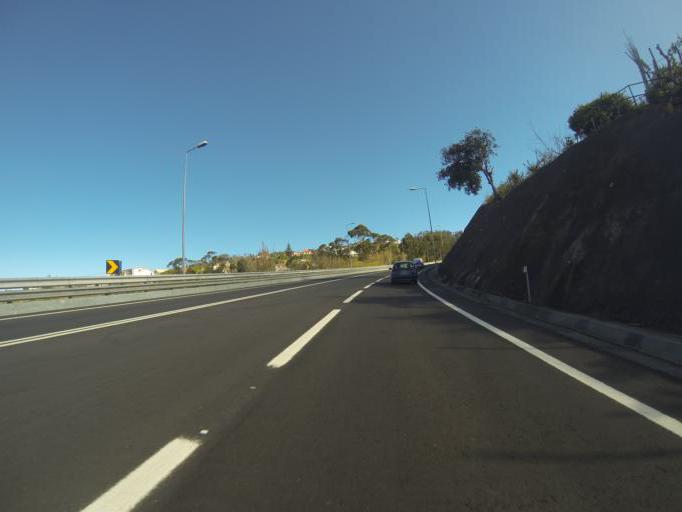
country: PT
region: Madeira
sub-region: Calheta
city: Estreito da Calheta
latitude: 32.7409
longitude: -17.1949
